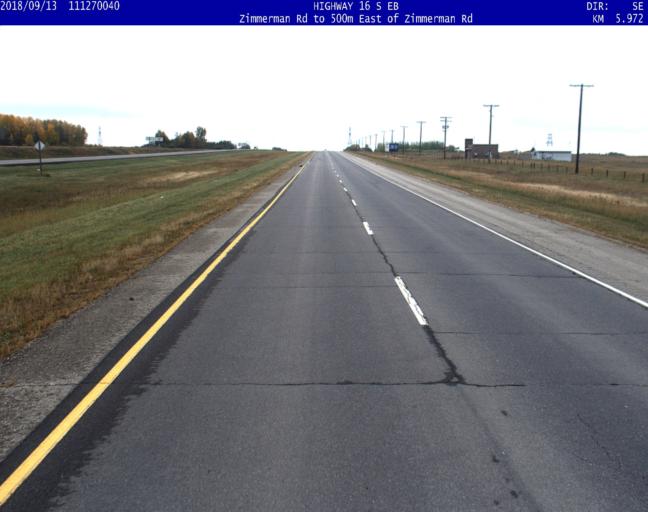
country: CA
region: Saskatchewan
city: Saskatoon
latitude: 52.0818
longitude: -106.5135
